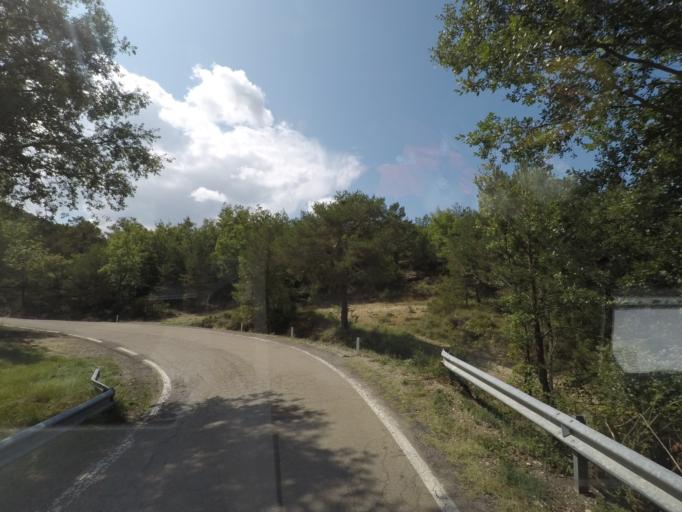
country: ES
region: Aragon
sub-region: Provincia de Huesca
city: Yebra de Basa
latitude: 42.3979
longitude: -0.3512
